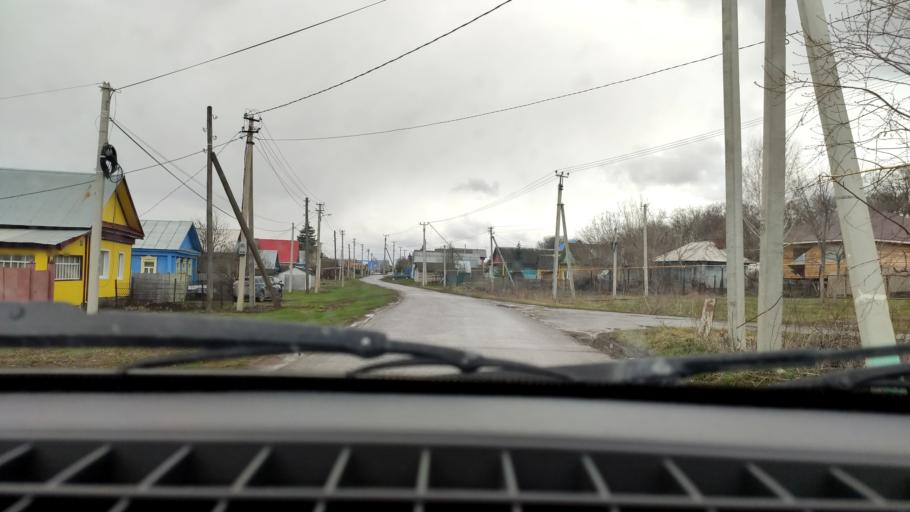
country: RU
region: Bashkortostan
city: Avdon
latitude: 54.6434
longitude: 55.7416
